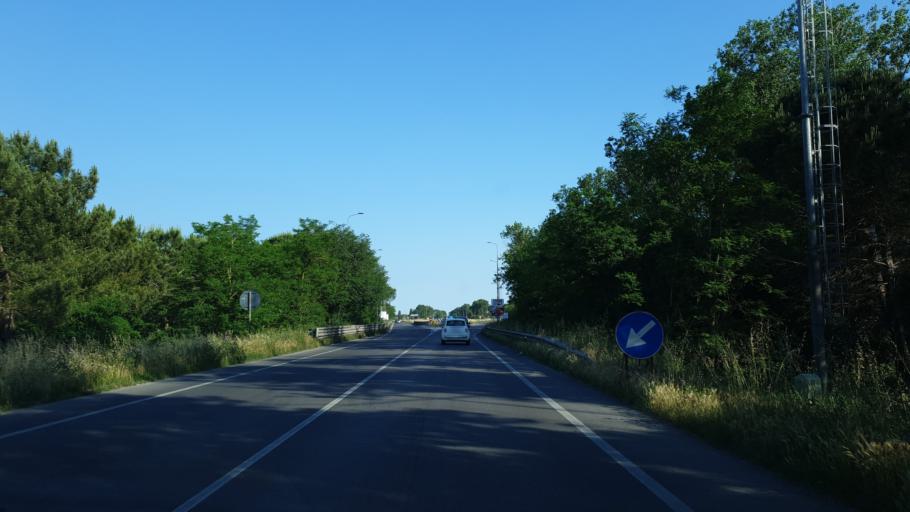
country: IT
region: Emilia-Romagna
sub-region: Provincia di Ravenna
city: Fosso Ghiaia
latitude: 44.3383
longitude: 12.2684
